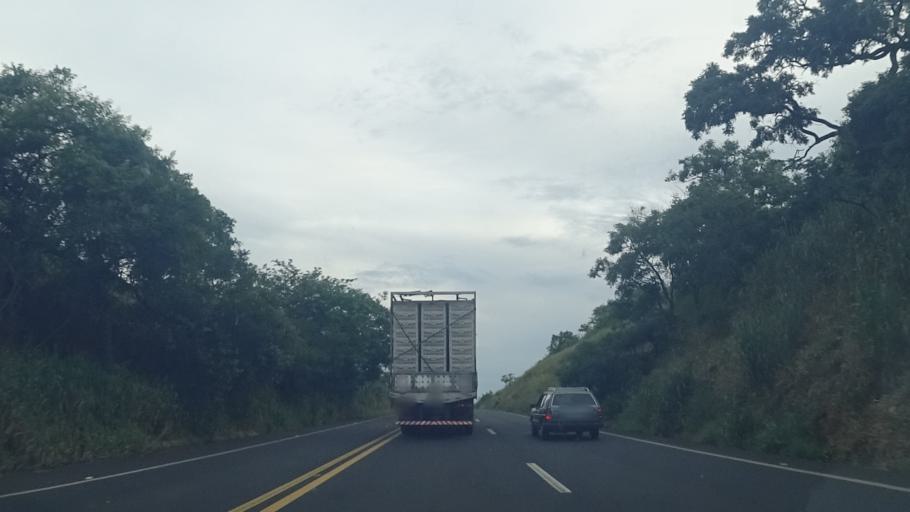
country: BR
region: Sao Paulo
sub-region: Martinopolis
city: Martinopolis
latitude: -22.1122
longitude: -51.1610
